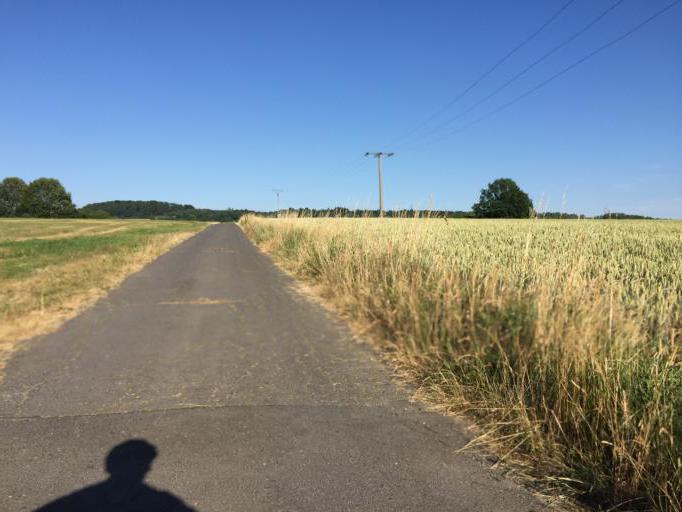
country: DE
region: Rheinland-Pfalz
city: Berod bei Wallmerod
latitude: 50.4792
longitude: 7.9409
